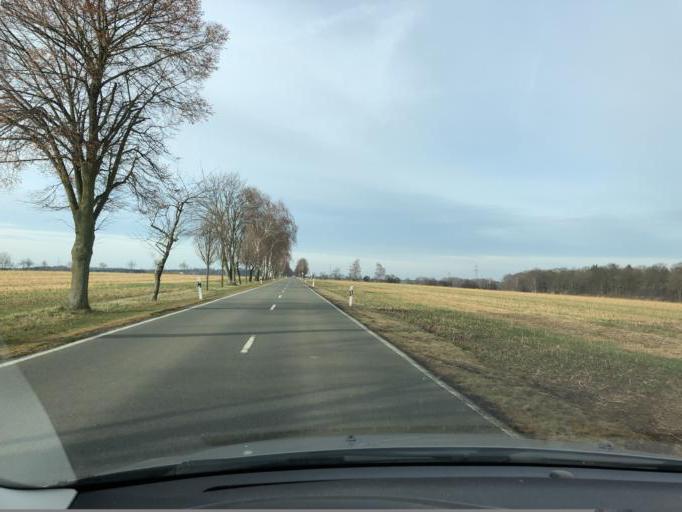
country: DE
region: Saxony-Anhalt
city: Bad Bibra
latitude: 51.1842
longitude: 11.5262
